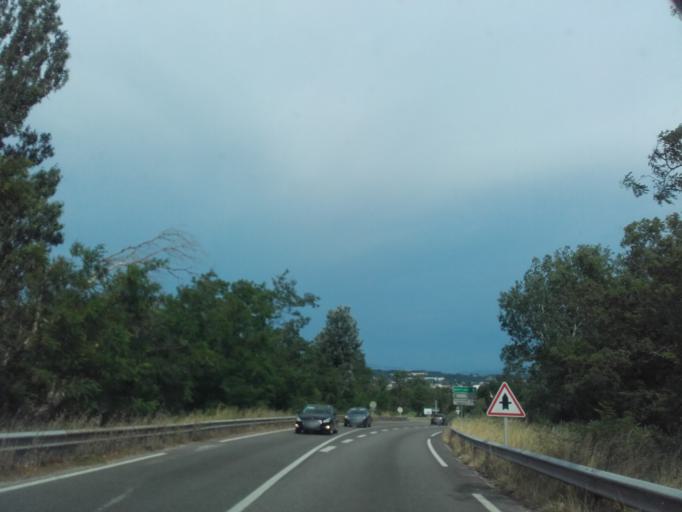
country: FR
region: Rhone-Alpes
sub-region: Departement de la Drome
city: Ancone
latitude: 44.5761
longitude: 4.7192
